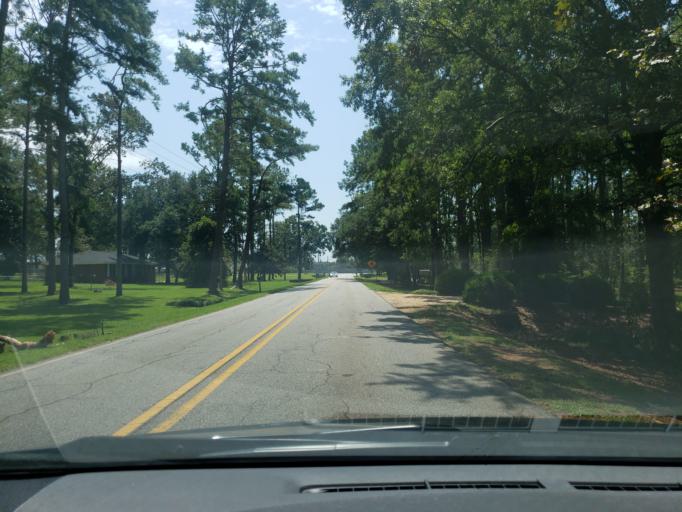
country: US
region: Georgia
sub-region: Dougherty County
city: Albany
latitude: 31.5884
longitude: -84.2808
